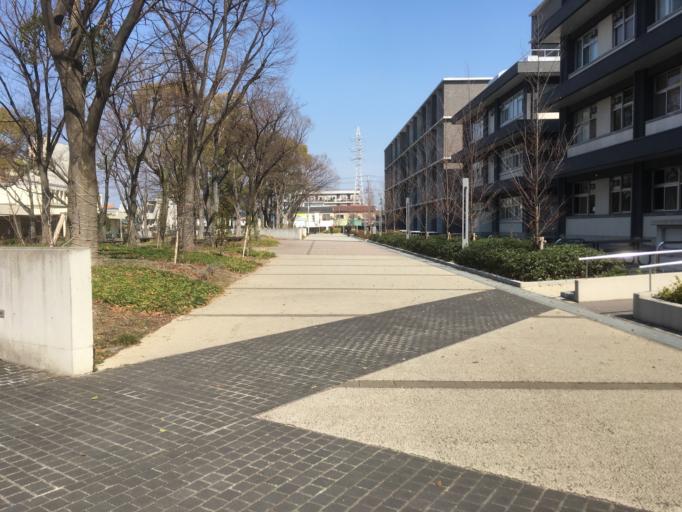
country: JP
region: Osaka
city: Sakai
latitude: 34.5930
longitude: 135.5054
